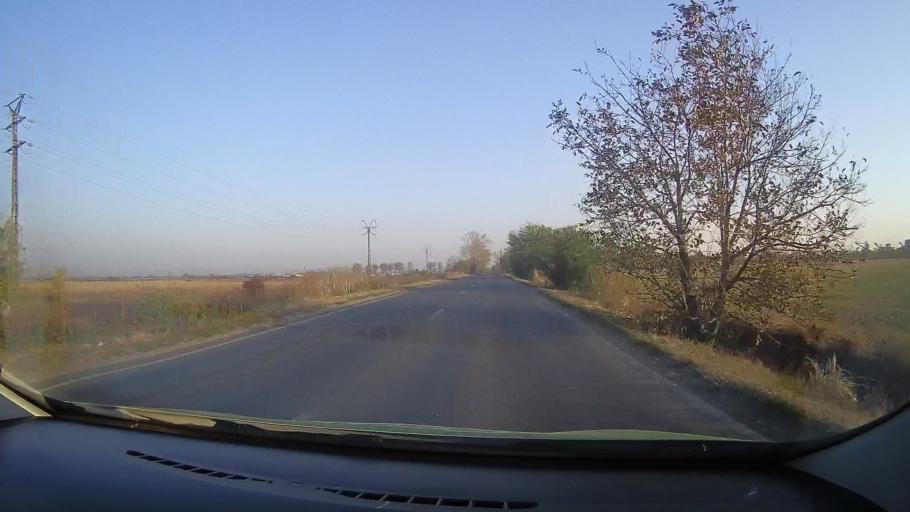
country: RO
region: Arad
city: Arad
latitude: 46.2205
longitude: 21.3205
